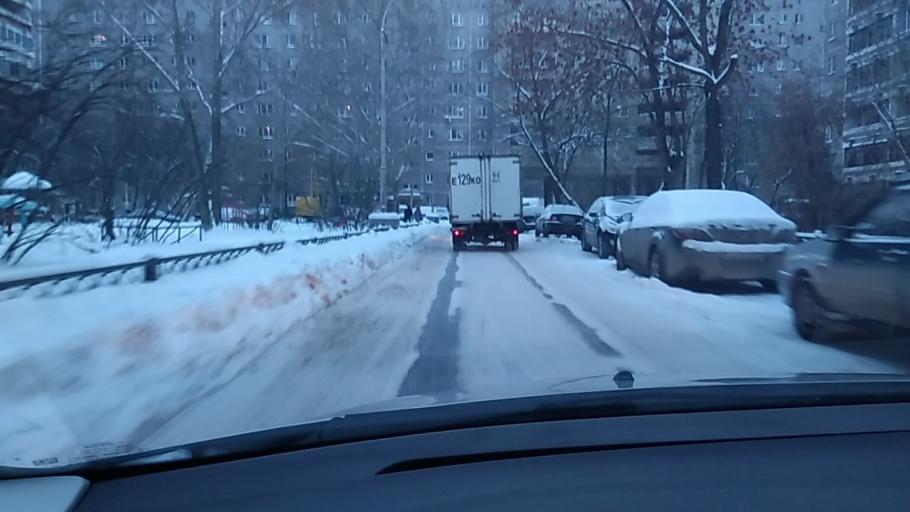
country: RU
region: Sverdlovsk
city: Yekaterinburg
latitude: 56.8928
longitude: 60.5963
